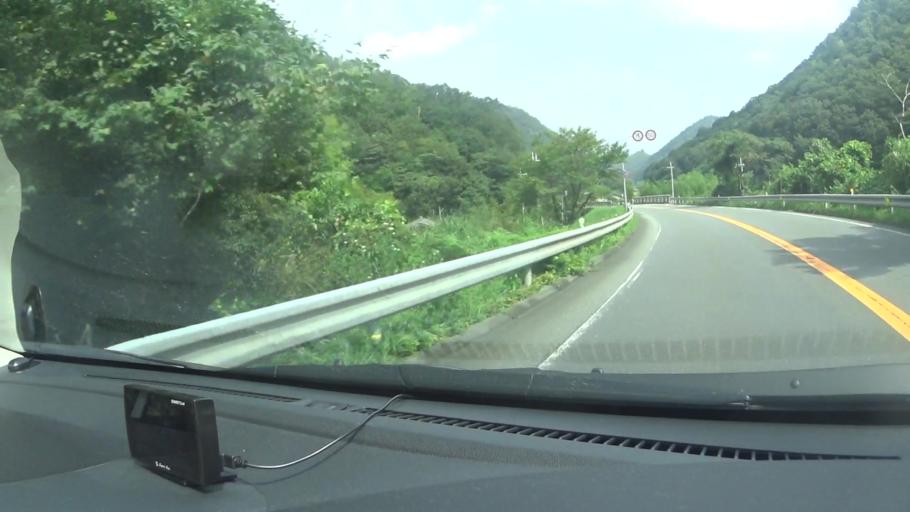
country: JP
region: Hyogo
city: Sasayama
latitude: 35.1451
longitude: 135.3548
